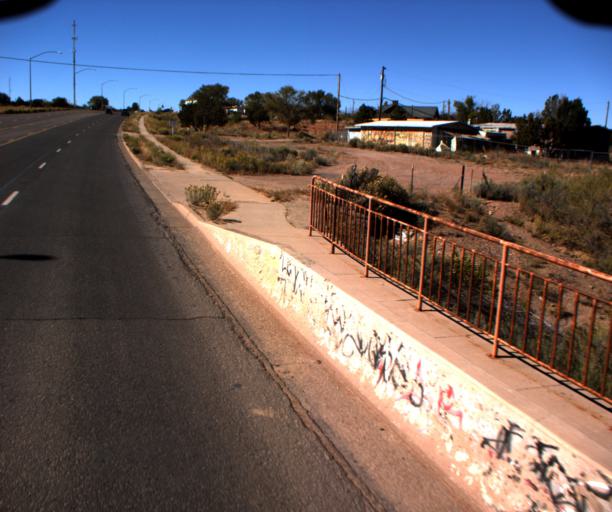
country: US
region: Arizona
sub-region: Apache County
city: Saint Michaels
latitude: 35.6555
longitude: -109.1051
